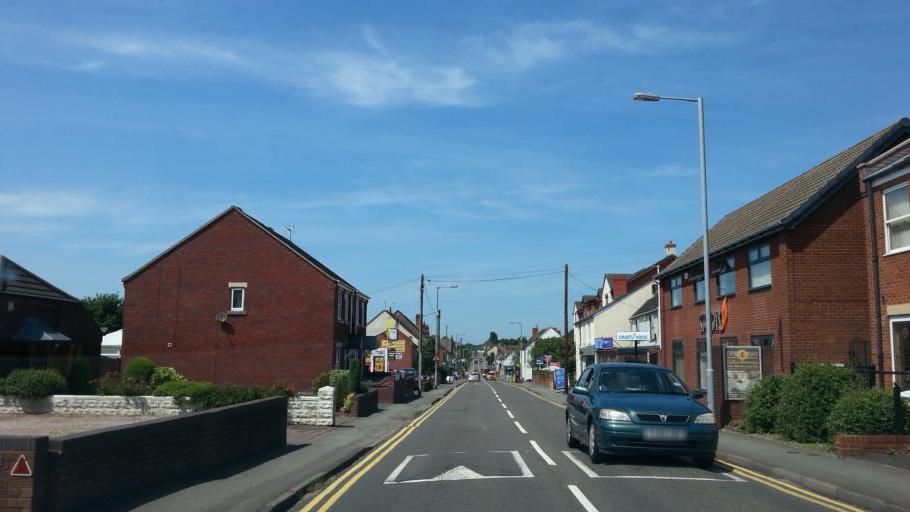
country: GB
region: England
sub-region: Staffordshire
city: Norton Canes
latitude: 52.6883
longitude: -1.9799
